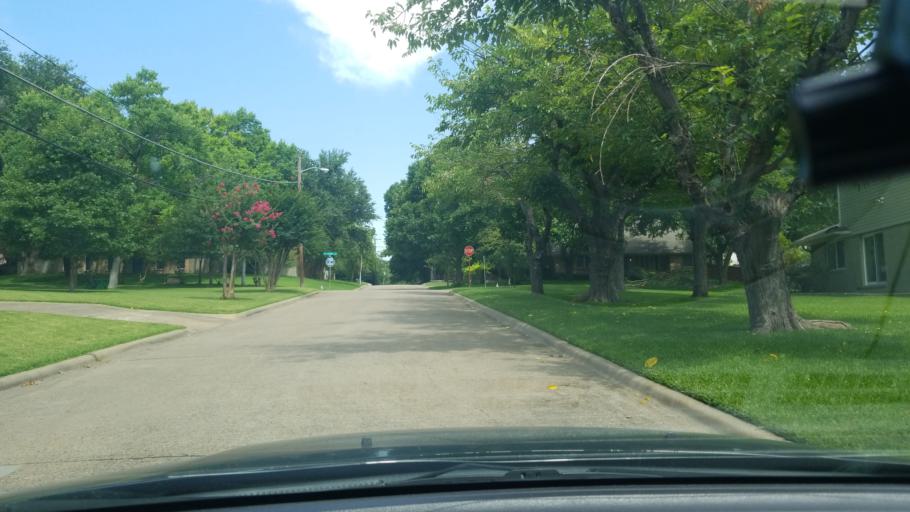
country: US
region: Texas
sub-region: Dallas County
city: Highland Park
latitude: 32.8095
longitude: -96.7153
